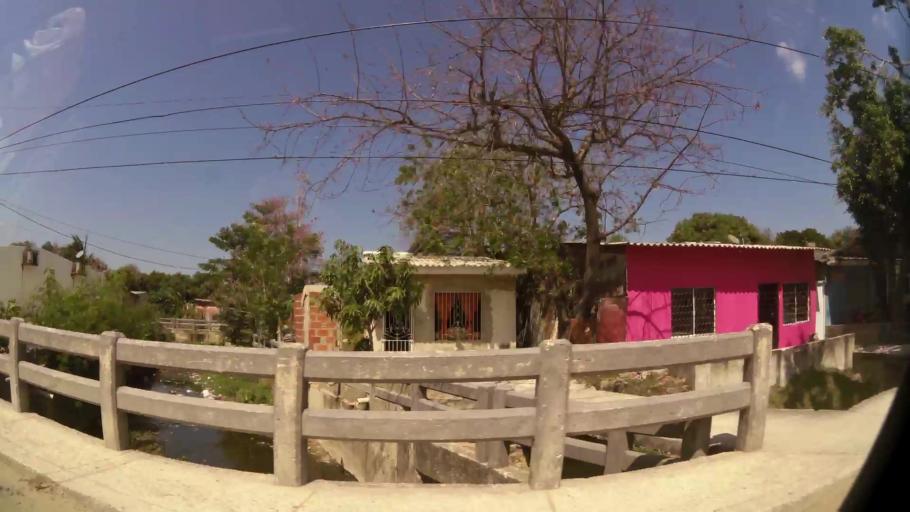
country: CO
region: Atlantico
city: Barranquilla
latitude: 10.9678
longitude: -74.8352
